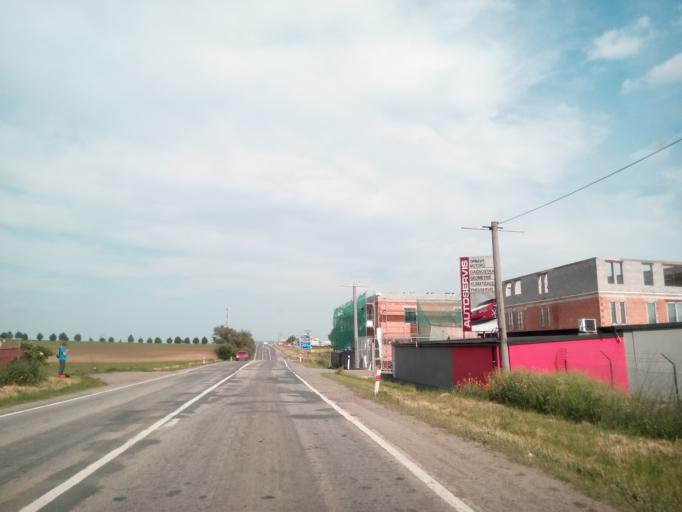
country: CZ
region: South Moravian
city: Blazovice
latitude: 49.1844
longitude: 16.8045
